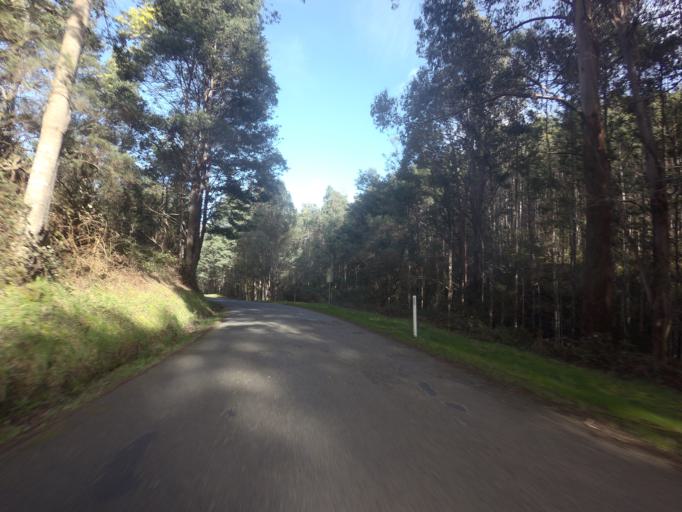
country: AU
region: Tasmania
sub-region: Huon Valley
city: Huonville
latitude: -43.0334
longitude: 147.1445
